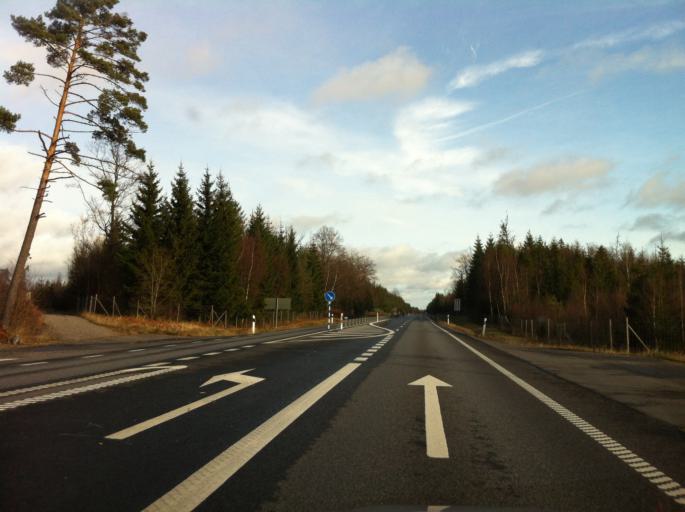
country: SE
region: Kronoberg
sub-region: Alvesta Kommun
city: Vislanda
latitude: 56.6887
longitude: 14.3253
